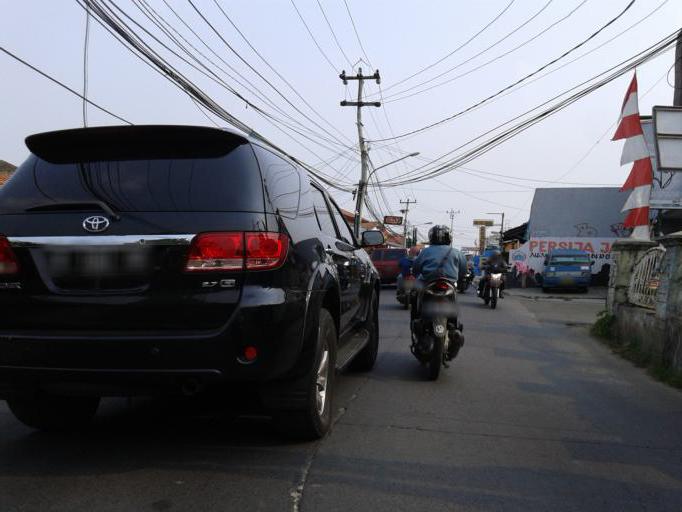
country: ID
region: West Java
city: Pamulang
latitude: -6.3594
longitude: 106.7757
